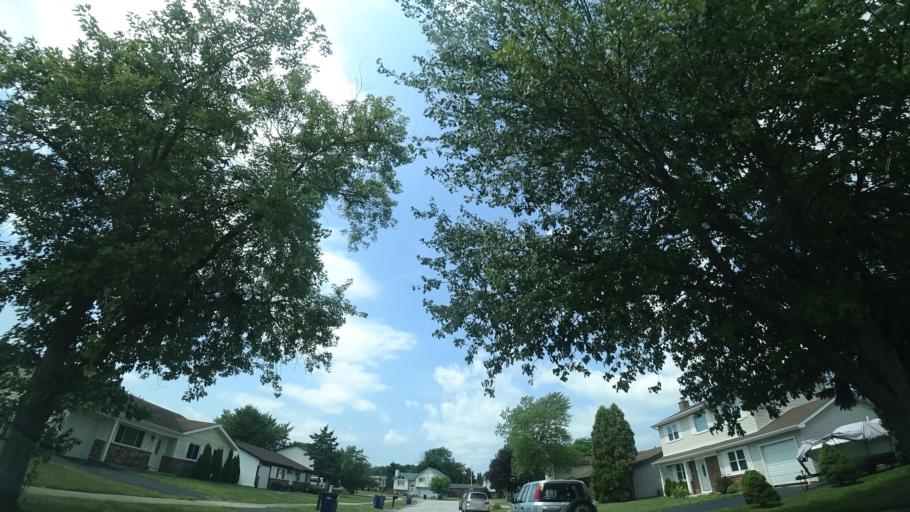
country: US
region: Illinois
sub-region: Will County
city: Frankfort Square
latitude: 41.5261
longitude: -87.7609
